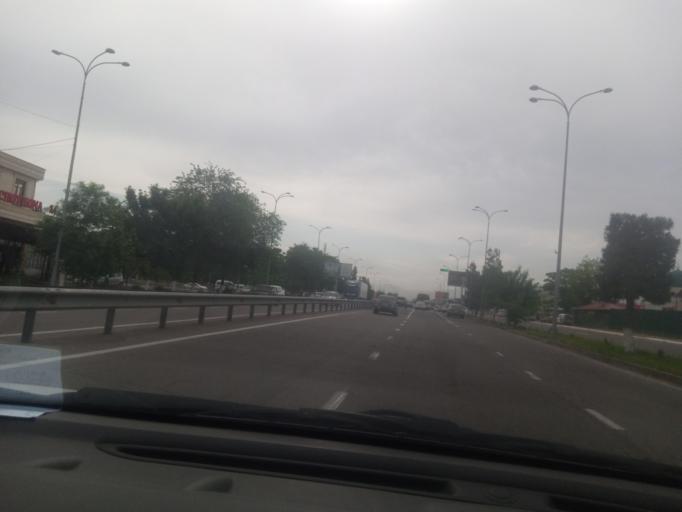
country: UZ
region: Toshkent
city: Ohangaron
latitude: 40.9045
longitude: 69.6380
